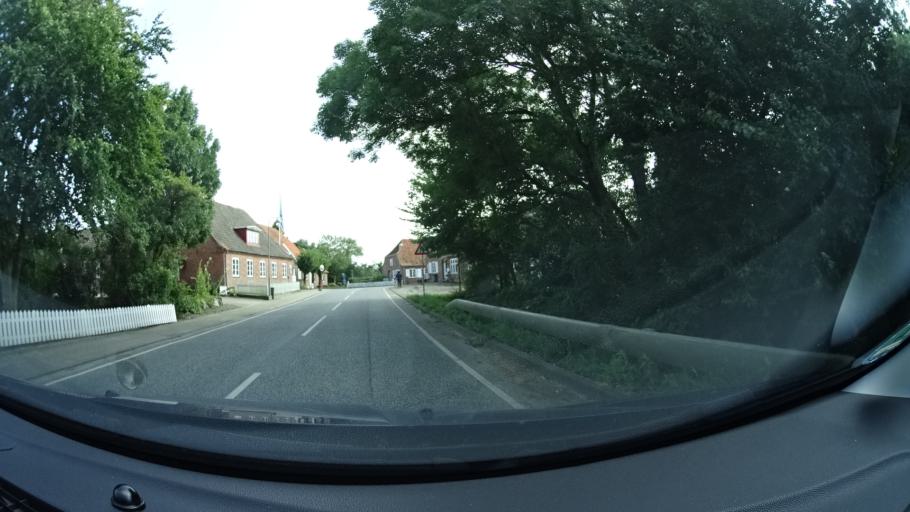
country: DE
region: Schleswig-Holstein
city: Neukirchen
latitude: 54.9009
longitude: 8.7533
